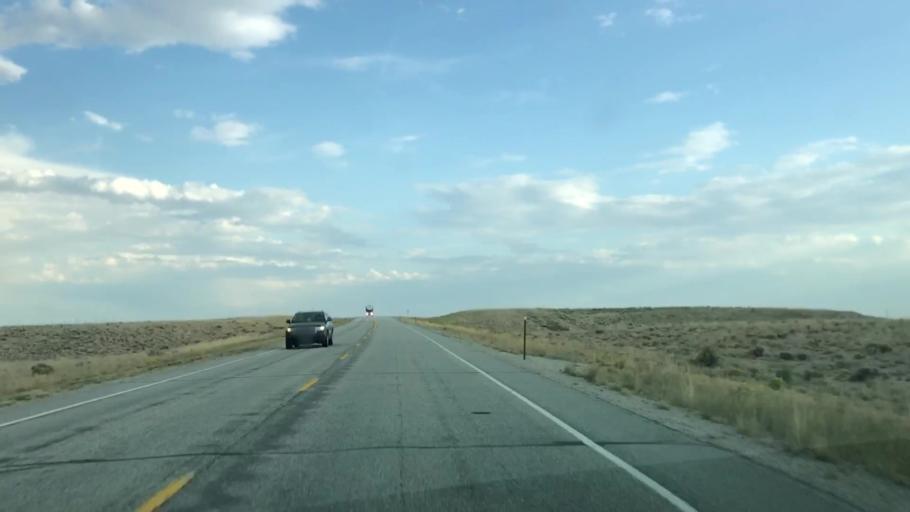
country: US
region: Wyoming
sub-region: Sweetwater County
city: North Rock Springs
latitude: 42.2794
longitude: -109.4849
